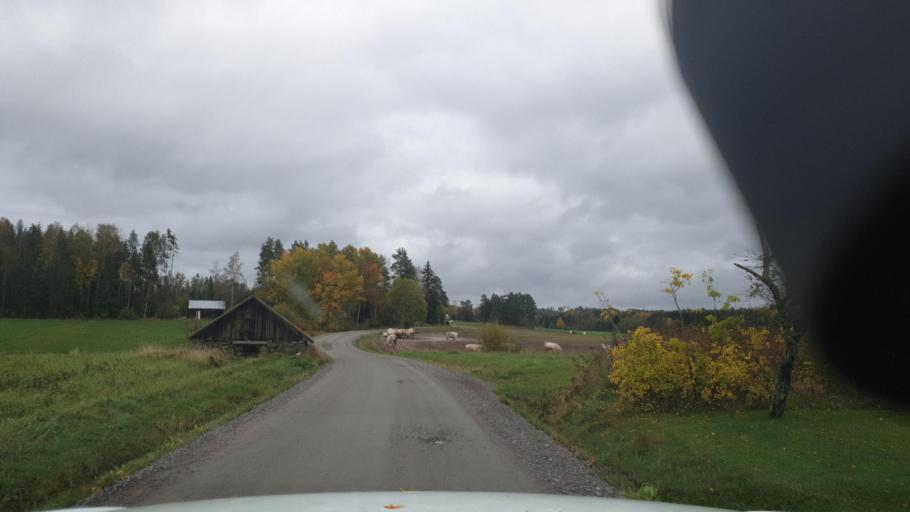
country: SE
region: Vaermland
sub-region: Karlstads Kommun
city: Edsvalla
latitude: 59.4962
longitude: 13.1822
